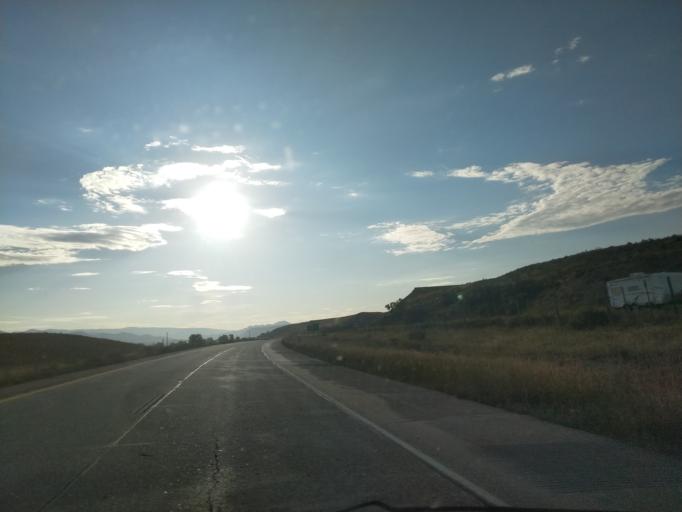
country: US
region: Colorado
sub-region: Garfield County
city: Rifle
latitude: 39.5297
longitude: -107.7387
